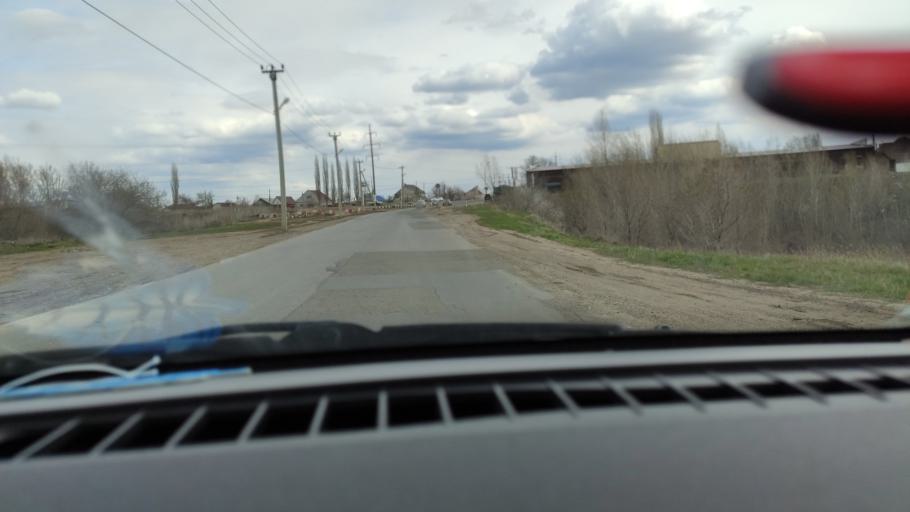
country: RU
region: Saratov
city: Engel's
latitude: 51.4599
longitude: 46.0906
